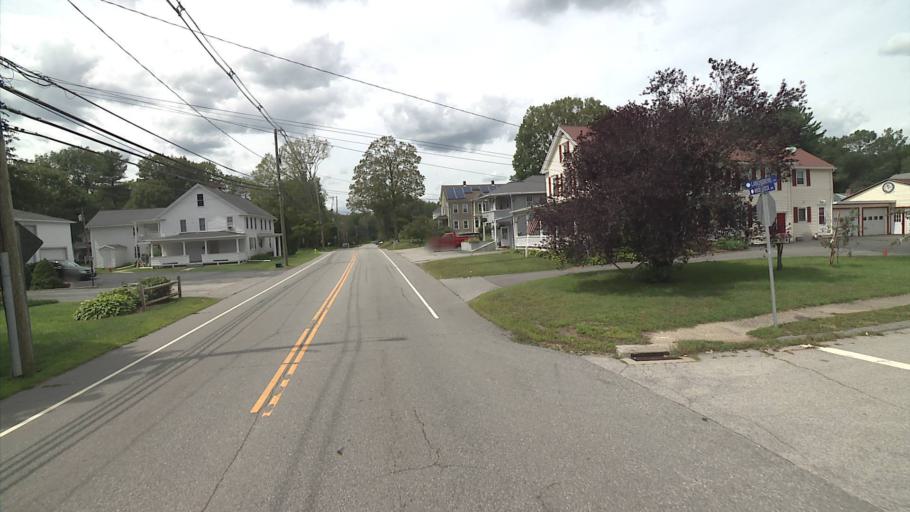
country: US
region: Connecticut
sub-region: Windham County
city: Putnam
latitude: 41.9289
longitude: -71.9237
